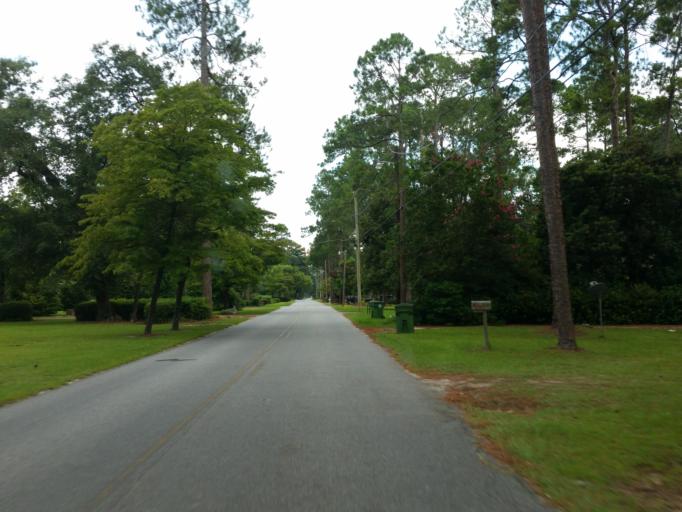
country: US
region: Georgia
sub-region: Cook County
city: Adel
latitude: 31.1313
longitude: -83.4180
